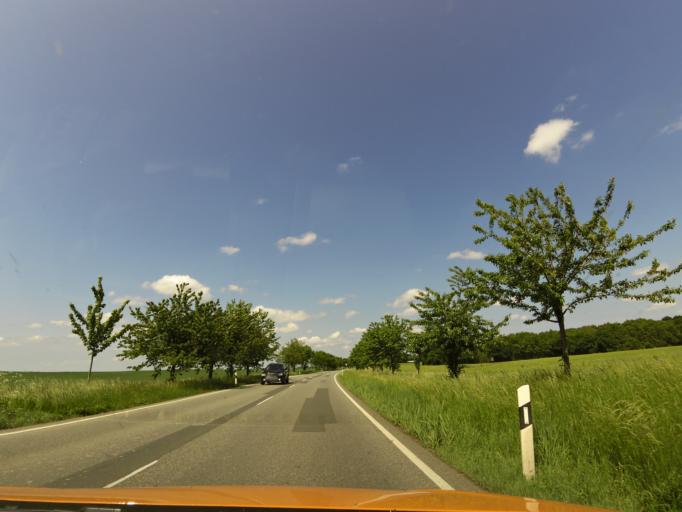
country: DE
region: Mecklenburg-Vorpommern
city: Gadebusch
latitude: 53.6761
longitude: 11.1448
